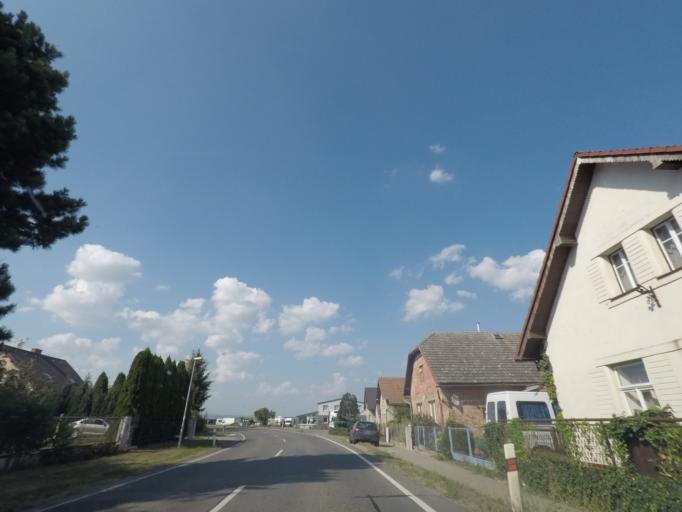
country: CZ
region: Kralovehradecky
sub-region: Okres Nachod
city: Jaromer
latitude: 50.3241
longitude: 15.9506
